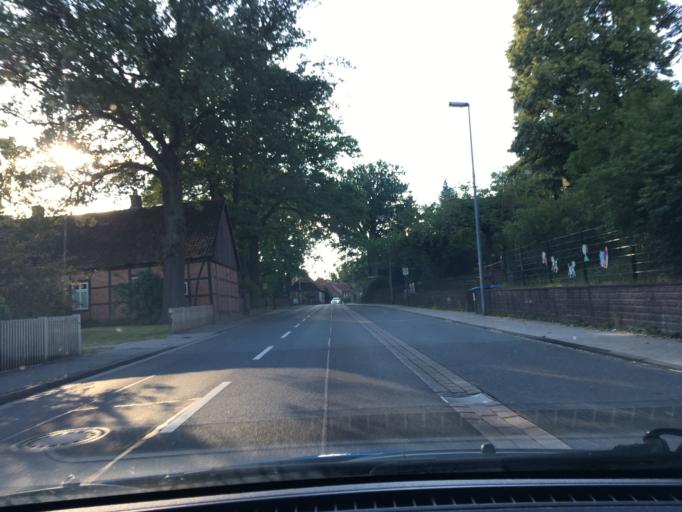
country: DE
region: Lower Saxony
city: Celle
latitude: 52.6332
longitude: 10.1142
